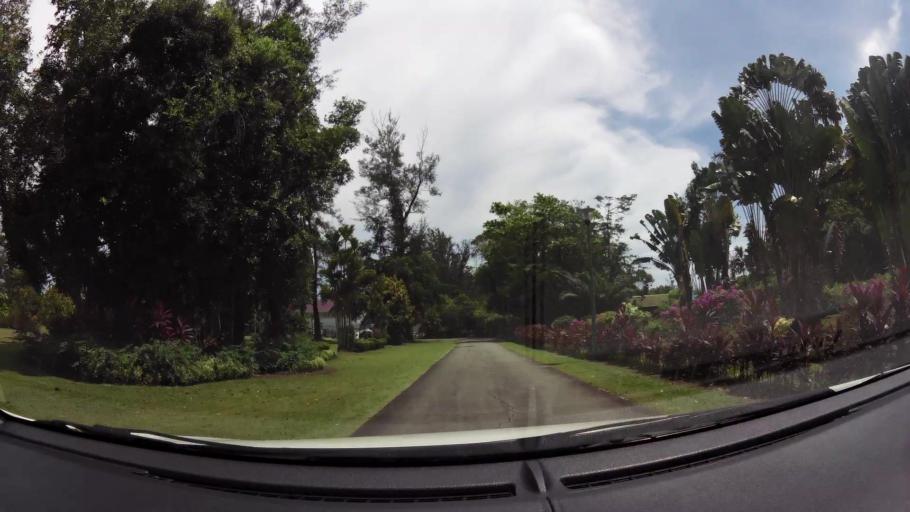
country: BN
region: Belait
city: Kuala Belait
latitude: 4.6011
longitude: 114.2737
